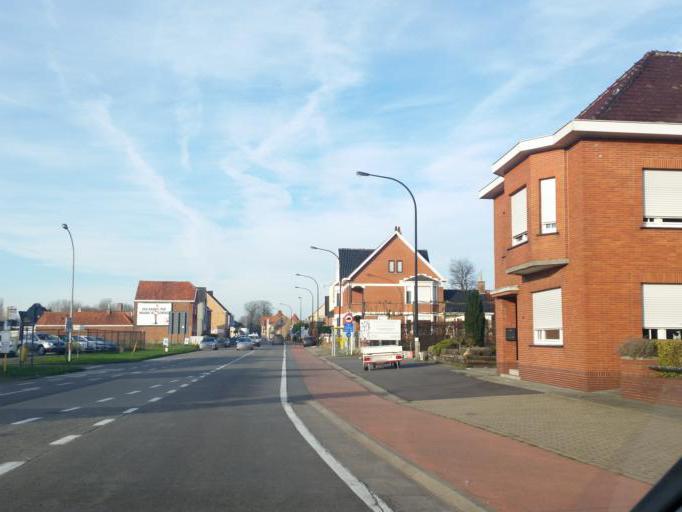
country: BE
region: Flanders
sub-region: Provincie Oost-Vlaanderen
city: Knesselare
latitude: 51.1359
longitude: 3.4230
